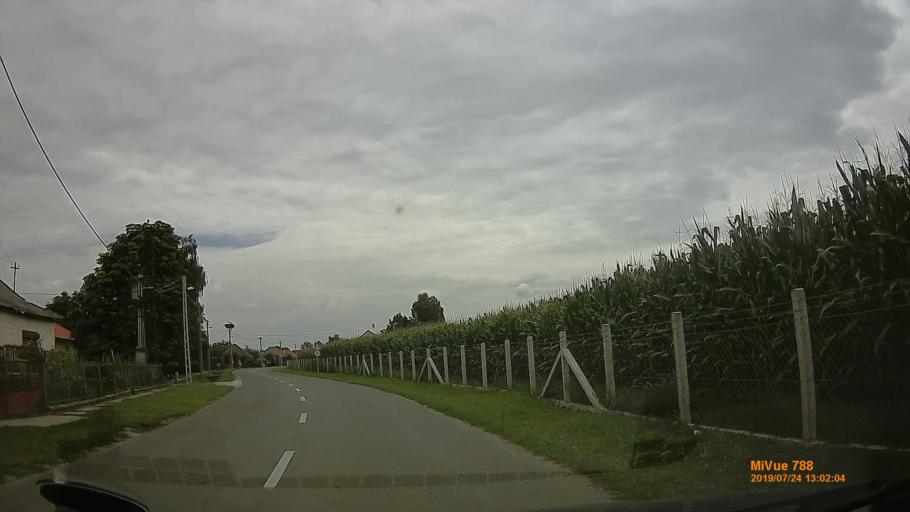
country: HU
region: Szabolcs-Szatmar-Bereg
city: Aranyosapati
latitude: 48.2243
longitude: 22.2912
